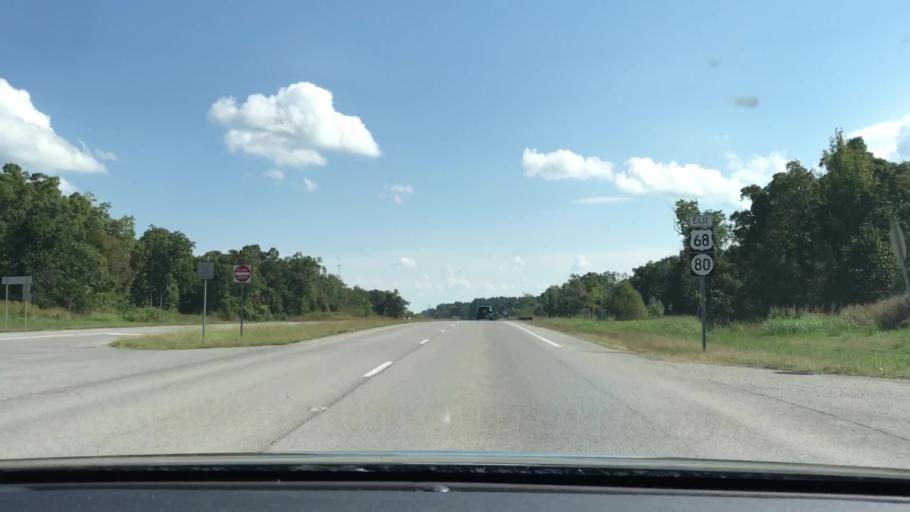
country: US
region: Kentucky
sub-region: Trigg County
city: Cadiz
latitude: 36.7785
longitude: -88.0773
